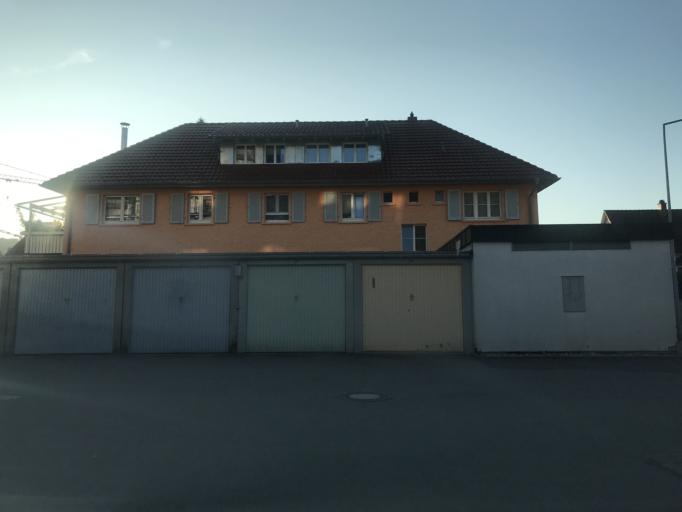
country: DE
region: Baden-Wuerttemberg
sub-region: Freiburg Region
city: Schopfheim
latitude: 47.6554
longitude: 7.8313
